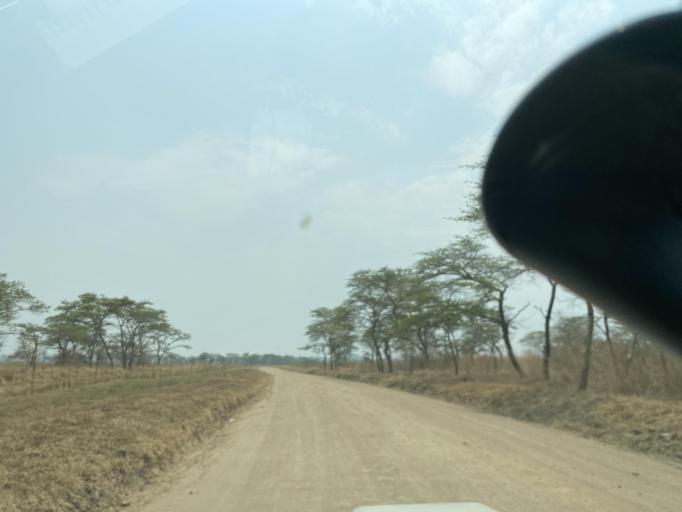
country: ZM
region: Lusaka
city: Kafue
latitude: -15.5851
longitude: 28.1181
